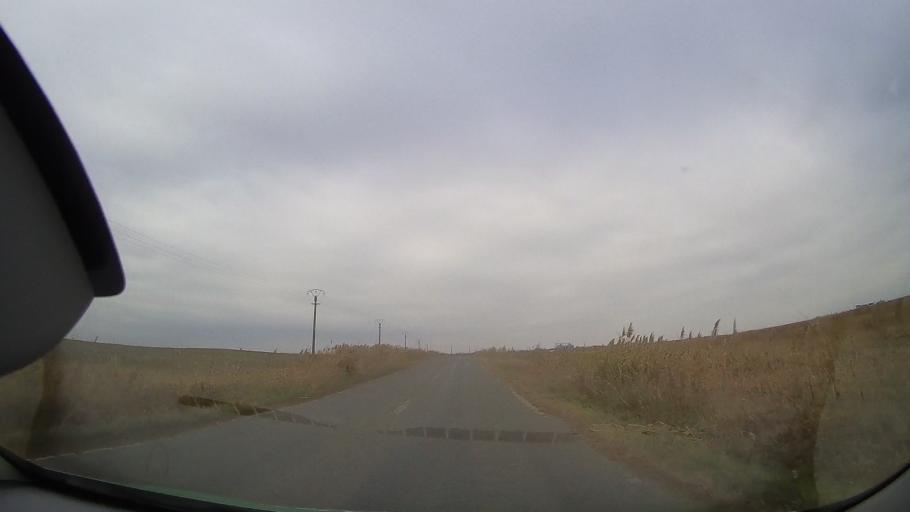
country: RO
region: Buzau
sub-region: Comuna Luciu
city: Luciu
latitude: 44.9667
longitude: 27.1093
